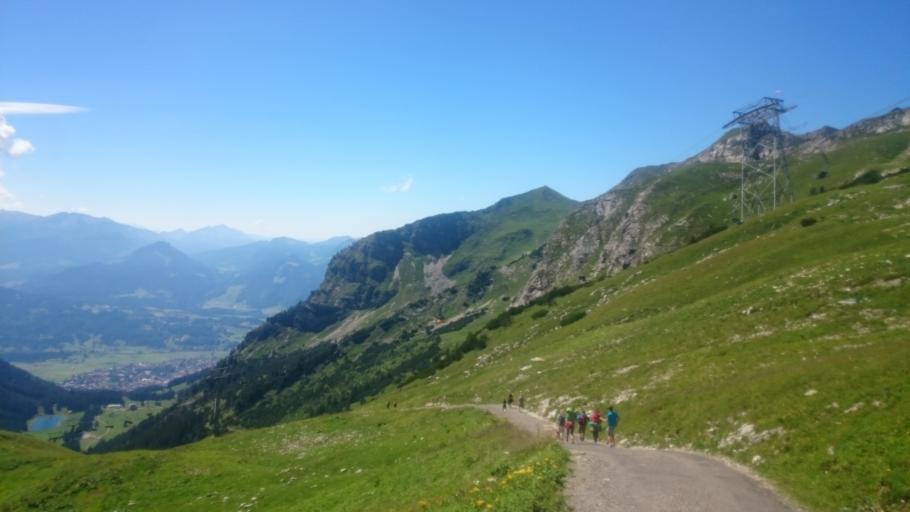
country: DE
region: Bavaria
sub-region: Swabia
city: Oberstdorf
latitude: 47.4124
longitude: 10.3465
